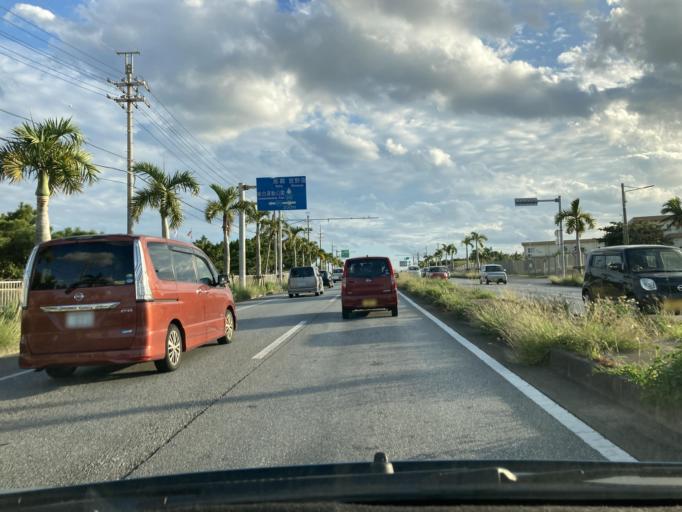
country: JP
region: Okinawa
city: Chatan
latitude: 26.2996
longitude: 127.7806
